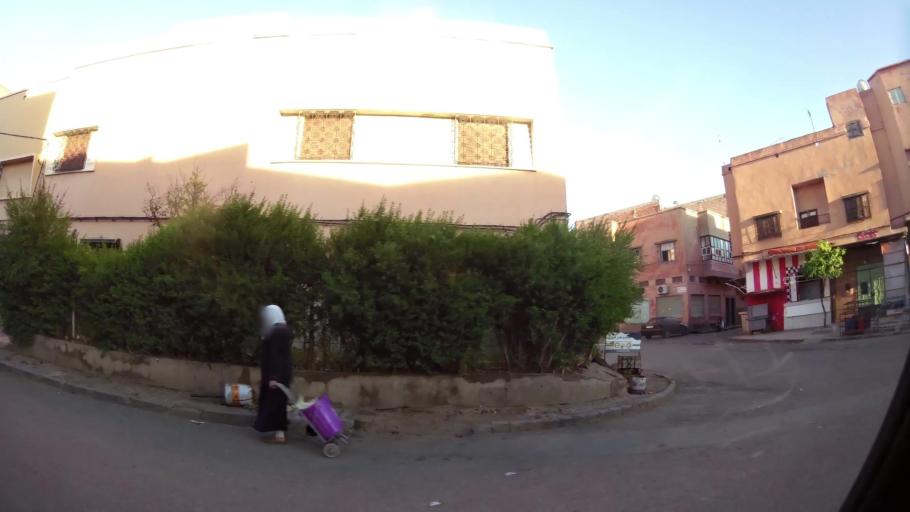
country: MA
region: Marrakech-Tensift-Al Haouz
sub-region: Marrakech
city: Marrakesh
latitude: 31.6251
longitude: -8.0355
